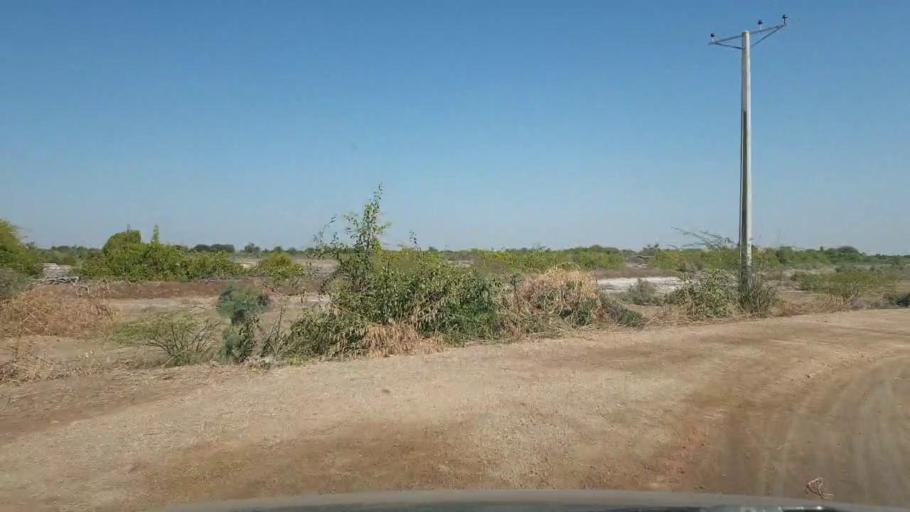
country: PK
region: Sindh
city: Dhoro Naro
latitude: 25.4134
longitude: 69.6196
